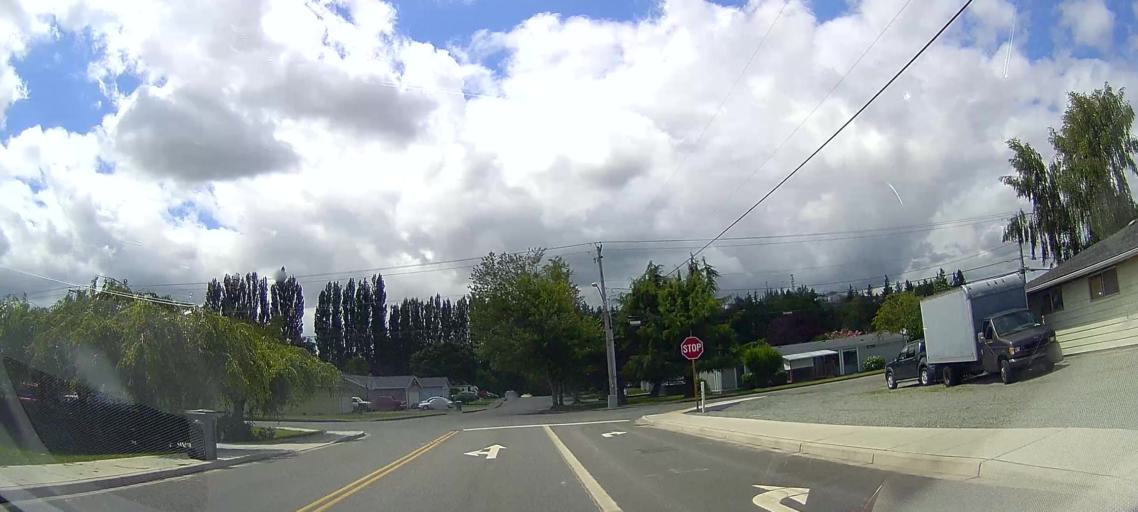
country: US
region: Washington
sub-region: Skagit County
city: Burlington
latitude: 48.4788
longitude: -122.3081
